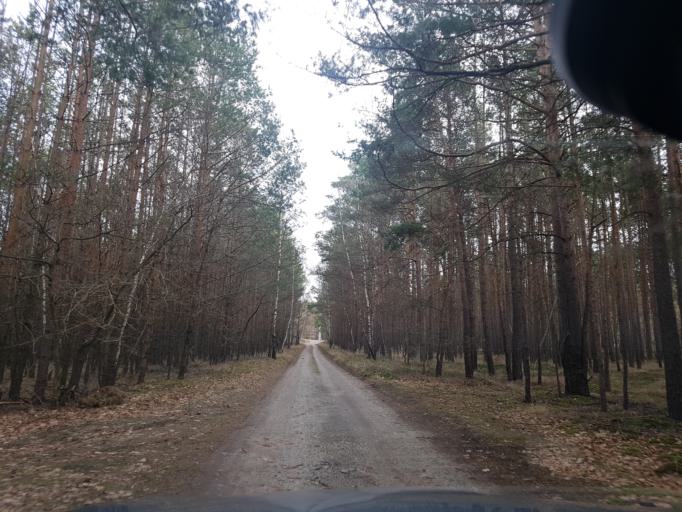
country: DE
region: Brandenburg
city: Doberlug-Kirchhain
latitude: 51.6294
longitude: 13.6019
